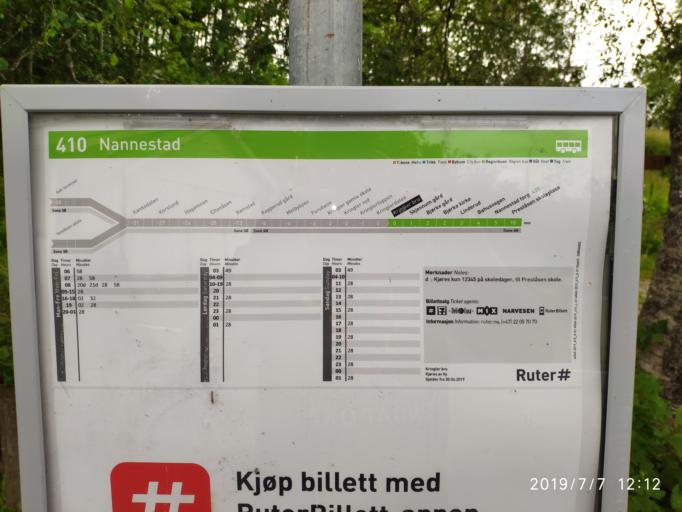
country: NO
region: Akershus
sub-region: Nannestad
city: Teigebyen
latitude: 60.2365
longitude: 10.9918
